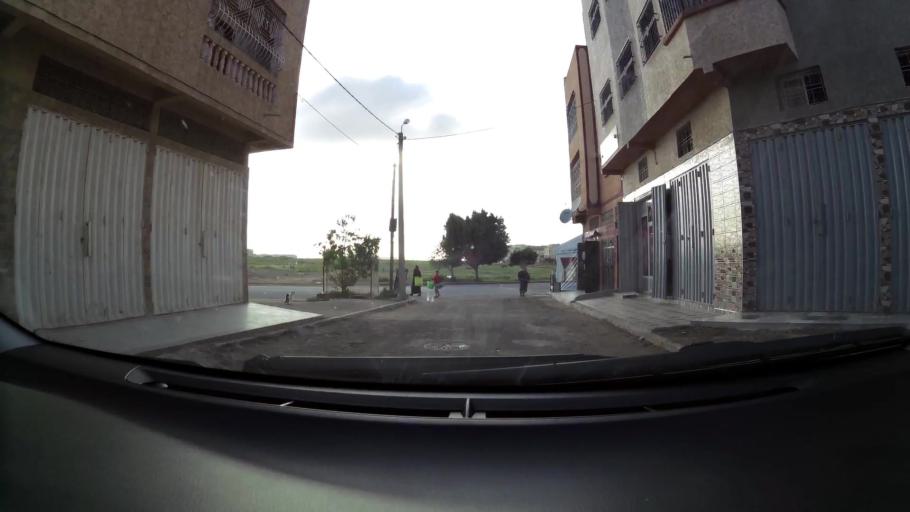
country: MA
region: Chaouia-Ouardigha
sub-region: Settat Province
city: Settat
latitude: 32.9986
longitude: -7.6354
